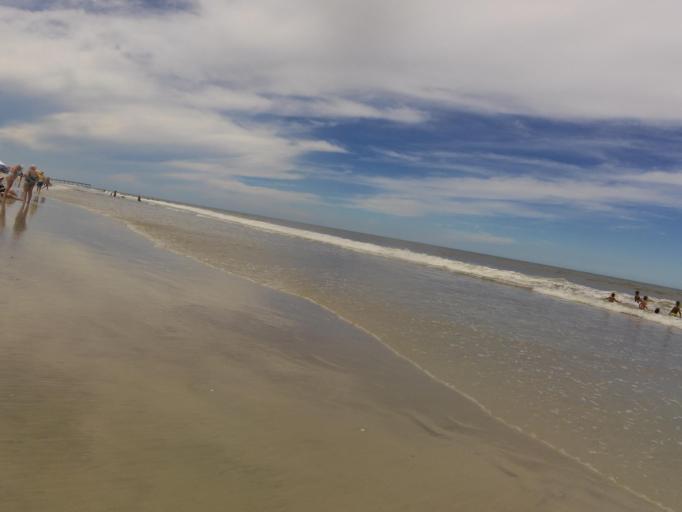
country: US
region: Florida
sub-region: Saint Johns County
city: Saint Augustine Beach
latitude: 29.8426
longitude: -81.2638
